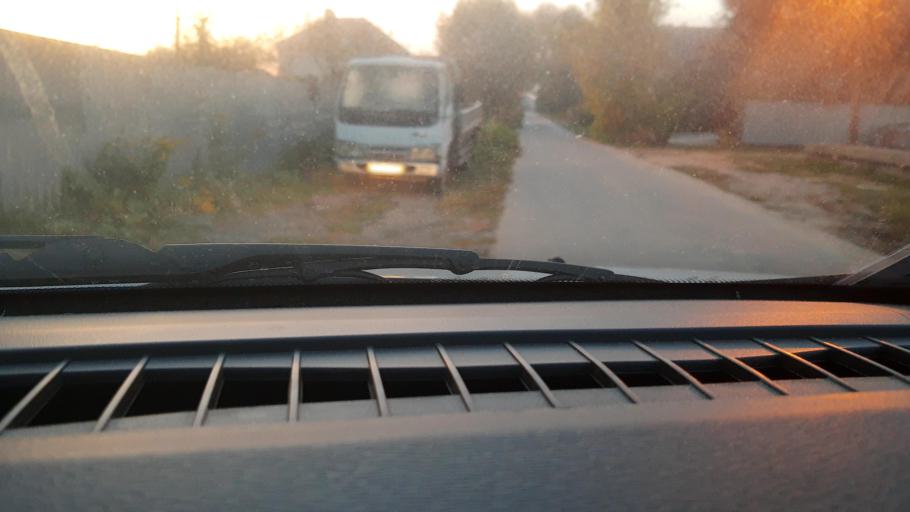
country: RU
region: Nizjnij Novgorod
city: Bor
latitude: 56.3812
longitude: 44.0357
